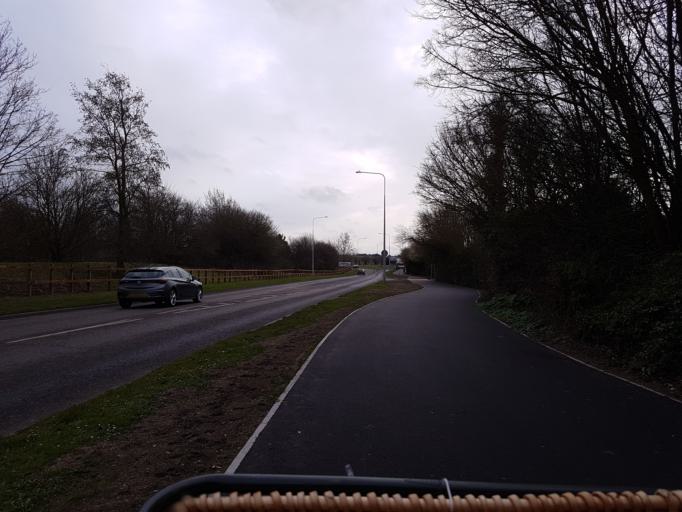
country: GB
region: England
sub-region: Cambridgeshire
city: Fulbourn
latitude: 52.1849
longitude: 0.1850
